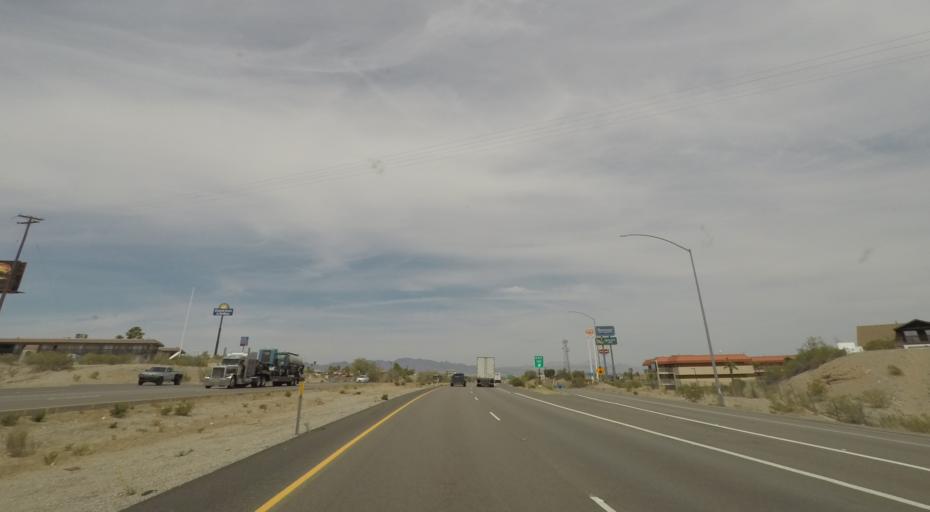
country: US
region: California
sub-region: San Bernardino County
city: Needles
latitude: 34.8366
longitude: -114.6099
